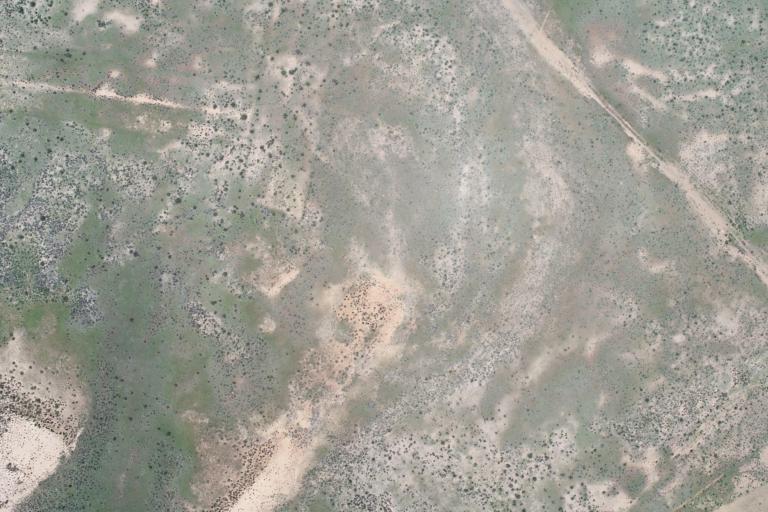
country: BO
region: La Paz
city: Patacamaya
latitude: -17.2737
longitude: -68.5077
